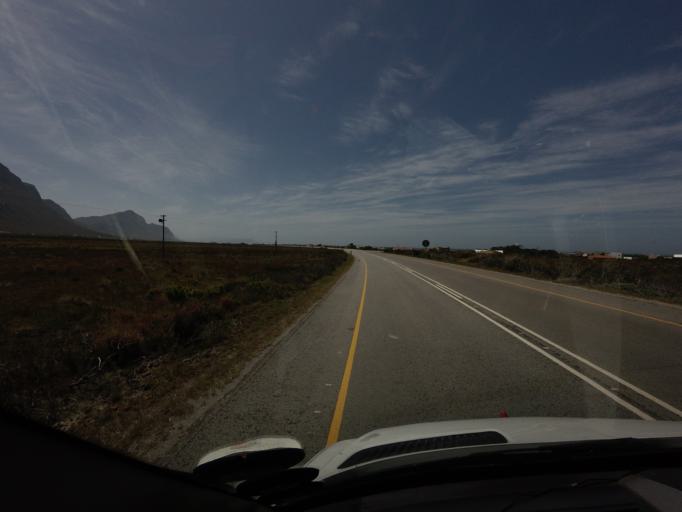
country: ZA
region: Western Cape
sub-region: Overberg District Municipality
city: Grabouw
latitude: -34.3606
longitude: 18.8655
